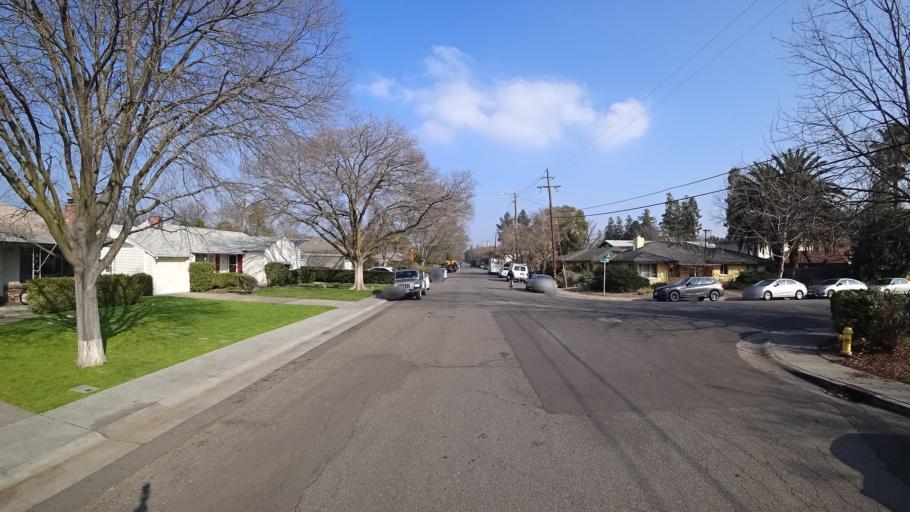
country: US
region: California
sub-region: Yolo County
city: Davis
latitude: 38.5522
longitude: -121.7449
